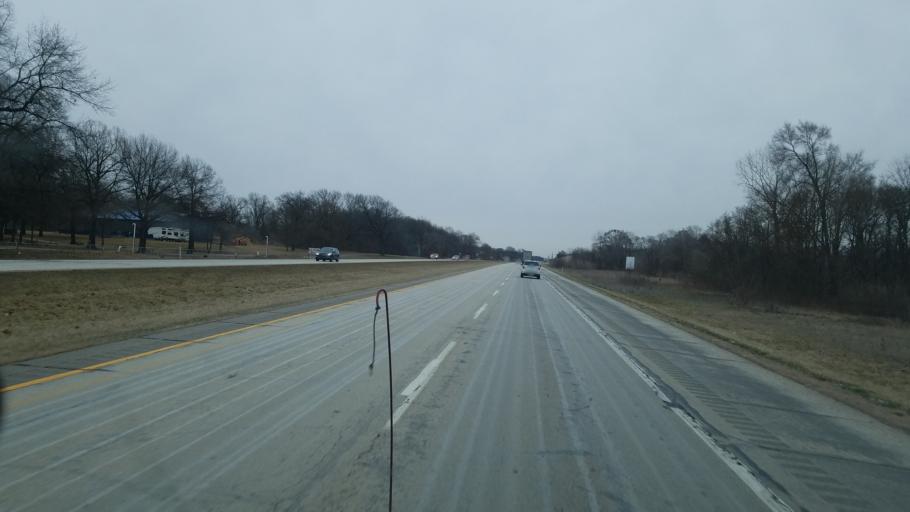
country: US
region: Indiana
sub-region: Starke County
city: Koontz Lake
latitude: 41.3727
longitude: -86.5161
